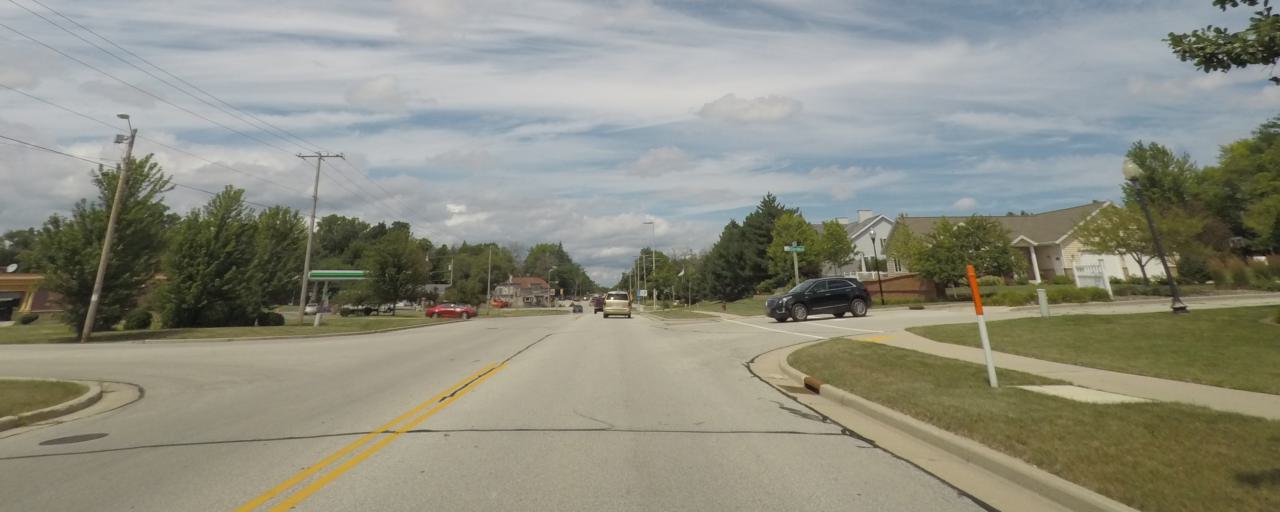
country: US
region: Wisconsin
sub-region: Milwaukee County
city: Hales Corners
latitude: 42.9621
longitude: -88.0692
